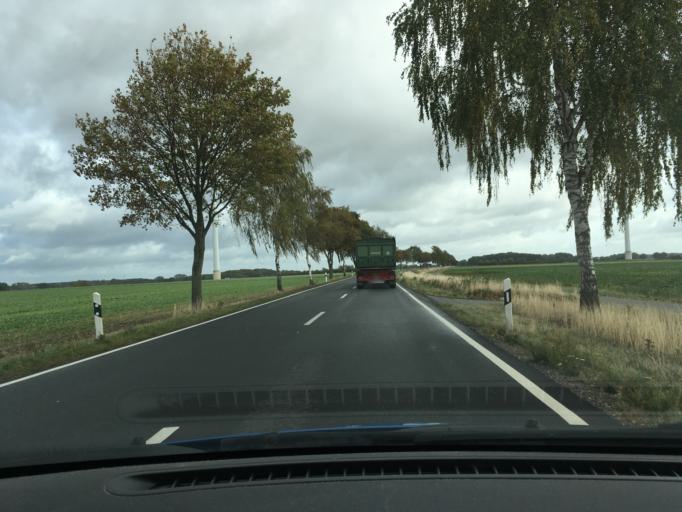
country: DE
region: Lower Saxony
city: Ratzlingen
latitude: 52.9578
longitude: 10.6387
